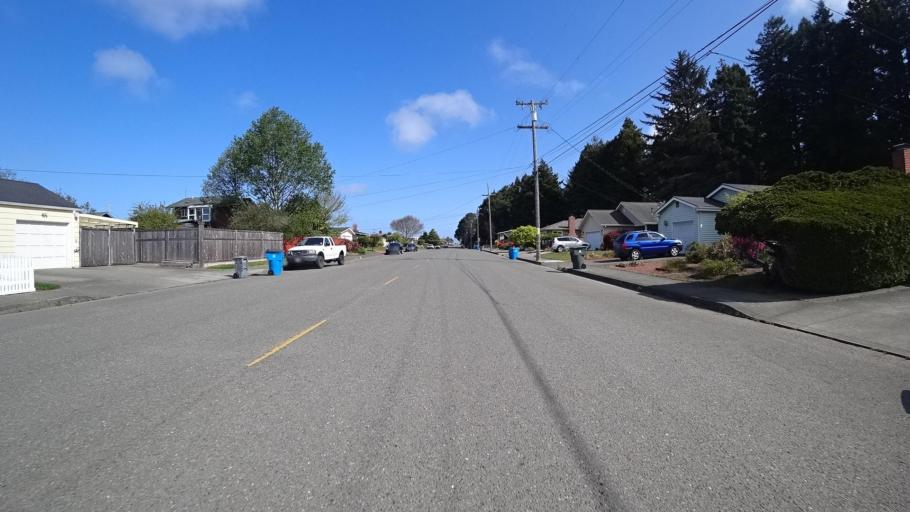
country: US
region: California
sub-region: Humboldt County
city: Cutten
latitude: 40.7762
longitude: -124.1602
